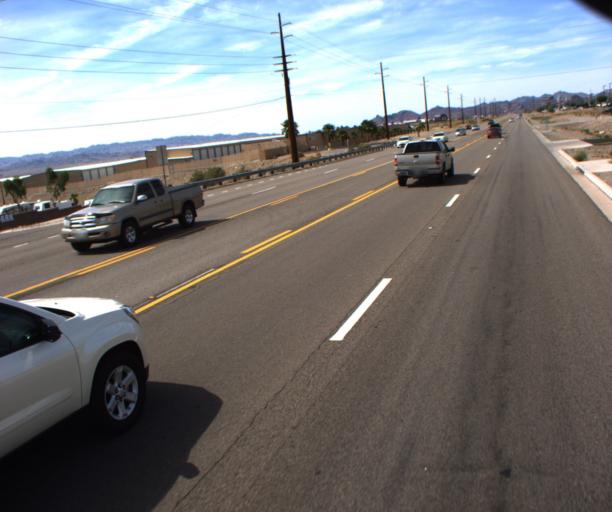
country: US
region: Arizona
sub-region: Mohave County
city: Desert Hills
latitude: 34.5385
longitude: -114.3523
